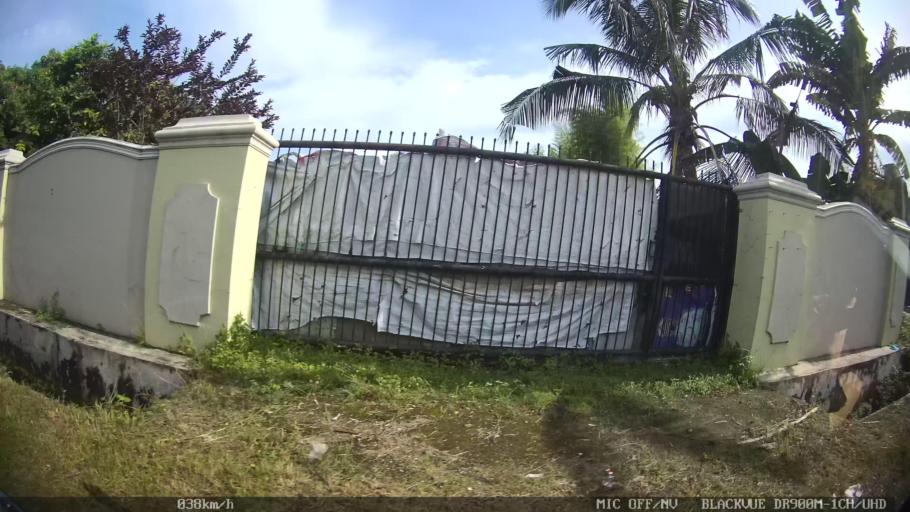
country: ID
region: North Sumatra
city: Medan
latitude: 3.6116
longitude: 98.6547
